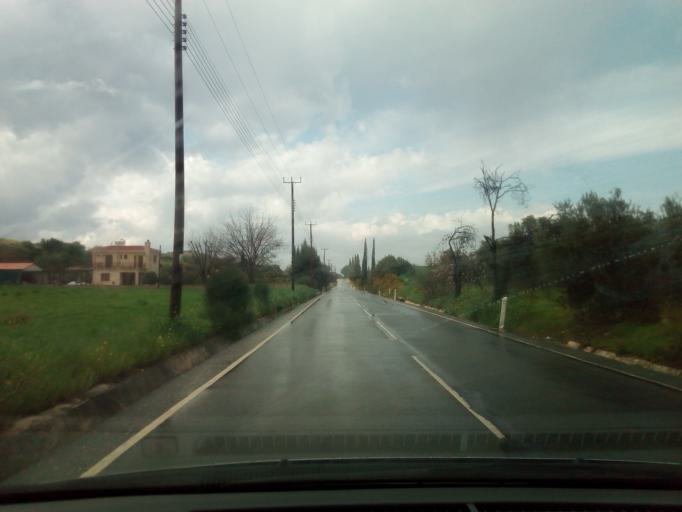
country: CY
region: Pafos
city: Polis
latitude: 35.0174
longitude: 32.4489
